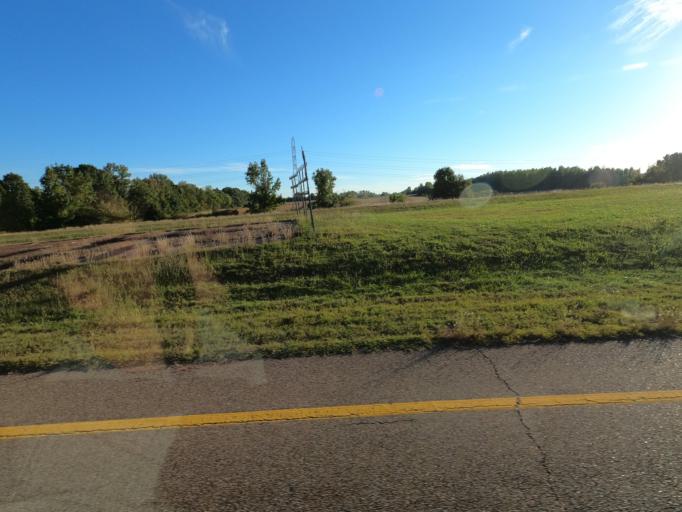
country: US
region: Tennessee
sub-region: Shelby County
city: Millington
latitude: 35.3311
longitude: -89.9171
